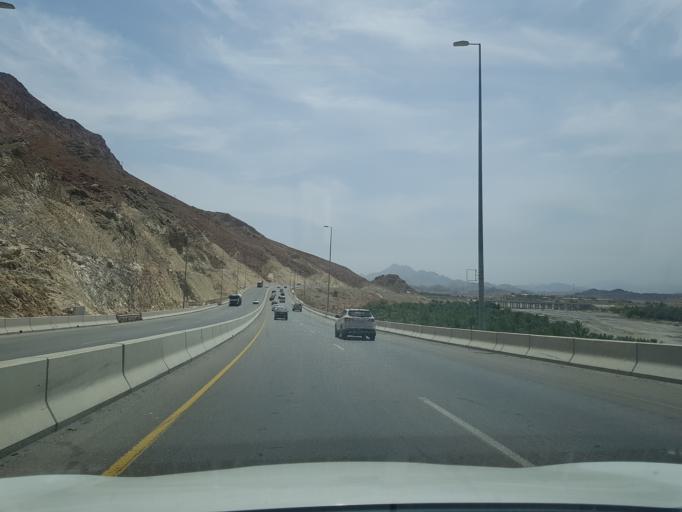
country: OM
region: Muhafazat ad Dakhiliyah
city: Bidbid
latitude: 23.4543
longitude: 58.1179
